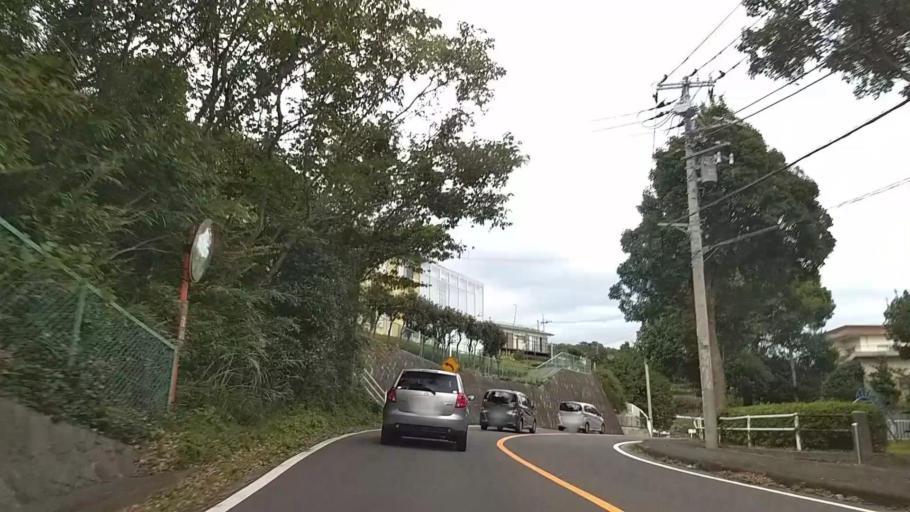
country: JP
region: Kanagawa
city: Yugawara
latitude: 35.1666
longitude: 139.1362
